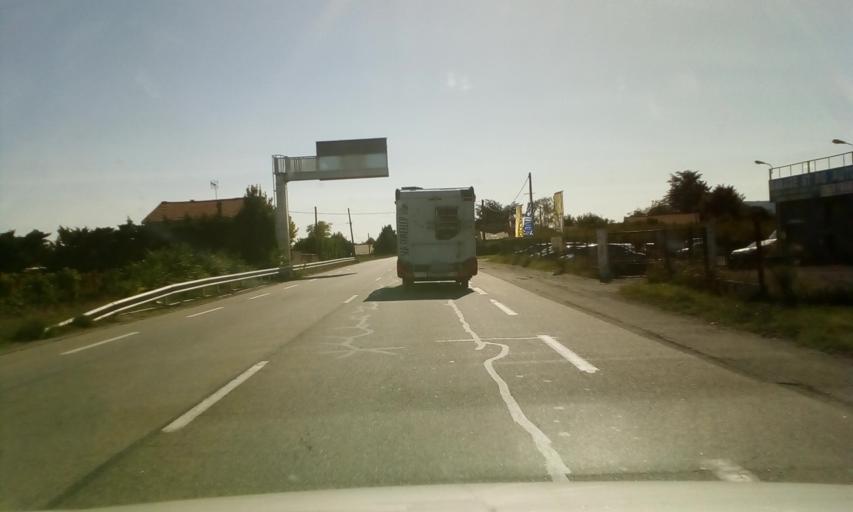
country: FR
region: Rhone-Alpes
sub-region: Departement de la Drome
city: La Roche-de-Glun
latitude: 45.0442
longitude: 4.8669
